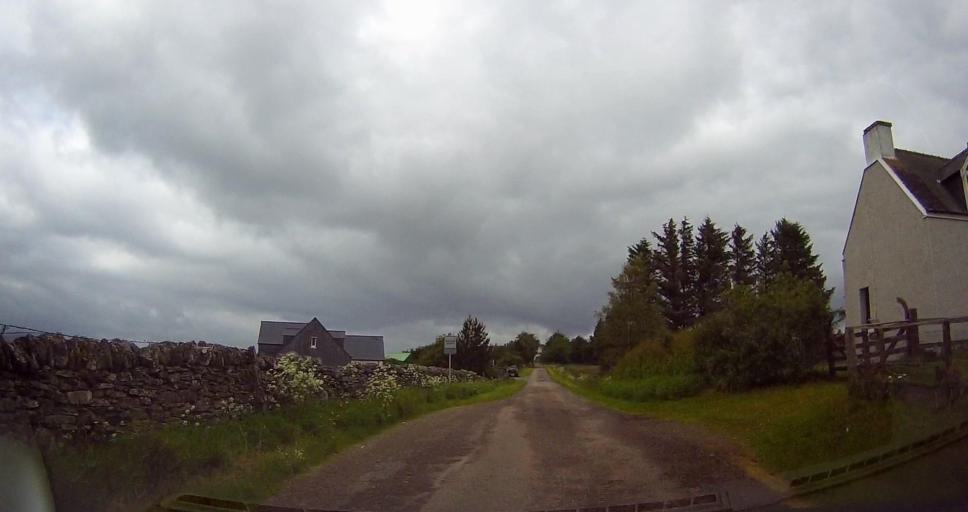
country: GB
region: Scotland
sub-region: Highland
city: Alness
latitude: 58.0740
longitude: -4.4386
